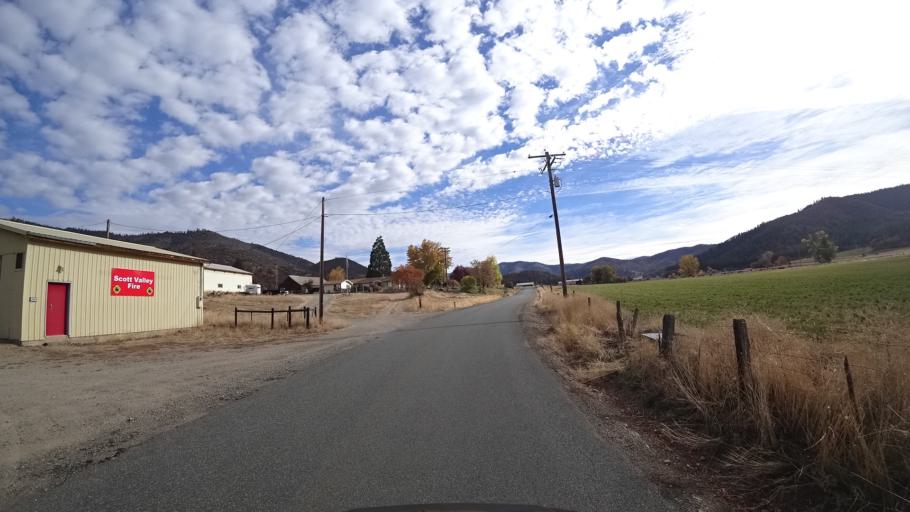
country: US
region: California
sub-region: Siskiyou County
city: Yreka
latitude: 41.6277
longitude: -122.8104
